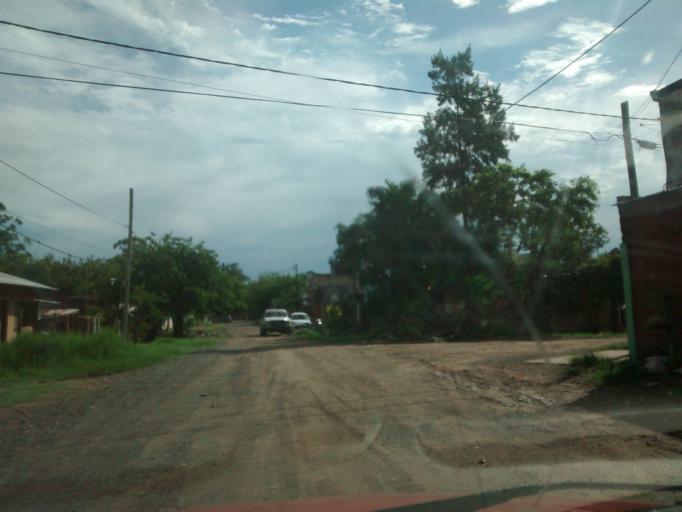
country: AR
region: Chaco
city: Resistencia
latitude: -27.4311
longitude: -58.9785
